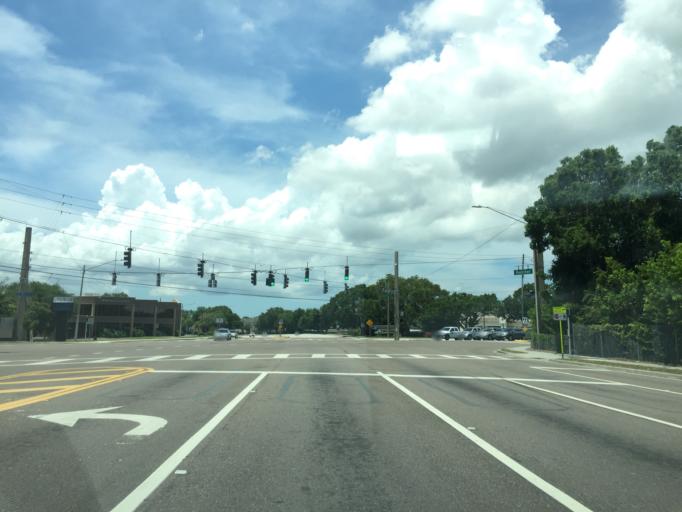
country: US
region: Florida
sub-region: Pinellas County
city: Dunedin
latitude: 27.9905
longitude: -82.7448
